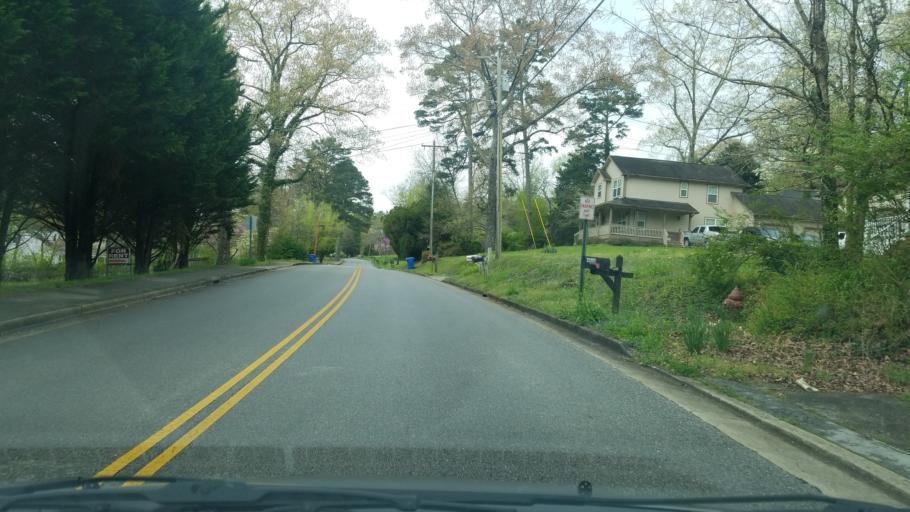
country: US
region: Tennessee
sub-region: Hamilton County
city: Collegedale
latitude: 35.0414
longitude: -85.0554
